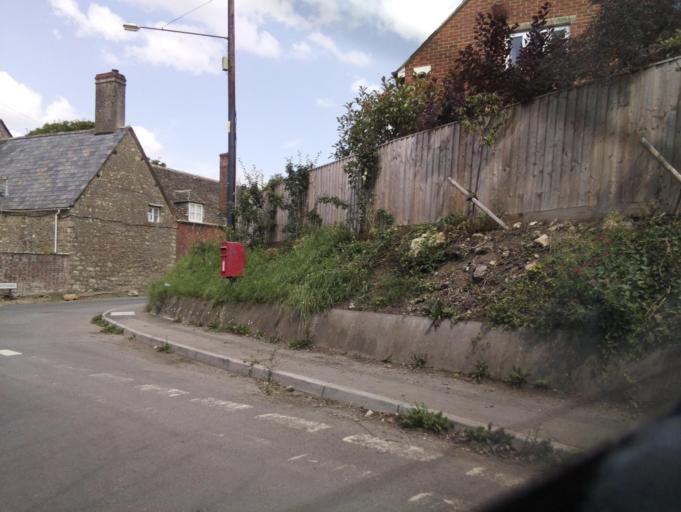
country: GB
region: England
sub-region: Wiltshire
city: Purton
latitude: 51.5871
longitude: -1.8894
